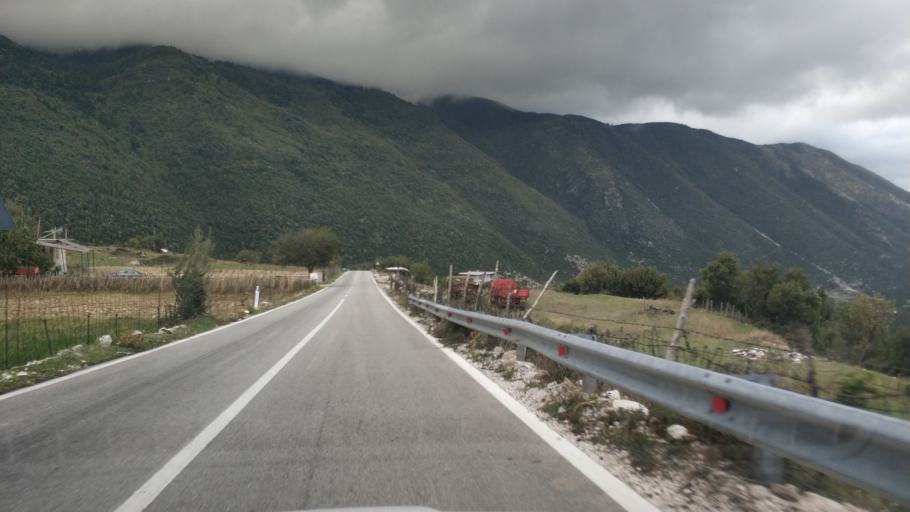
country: AL
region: Vlore
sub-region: Rrethi i Vlores
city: Brataj
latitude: 40.2306
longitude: 19.5750
